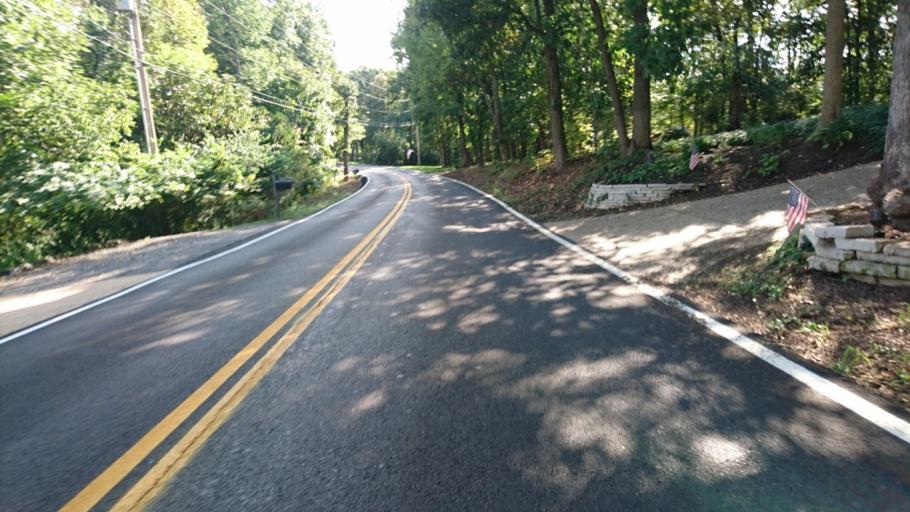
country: US
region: Missouri
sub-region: Saint Louis County
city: Eureka
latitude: 38.5362
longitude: -90.6395
